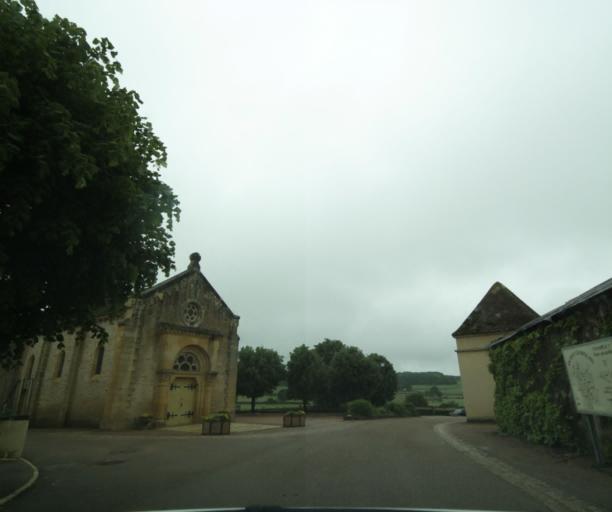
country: FR
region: Bourgogne
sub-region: Departement de Saone-et-Loire
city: Charolles
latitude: 46.4697
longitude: 4.2437
